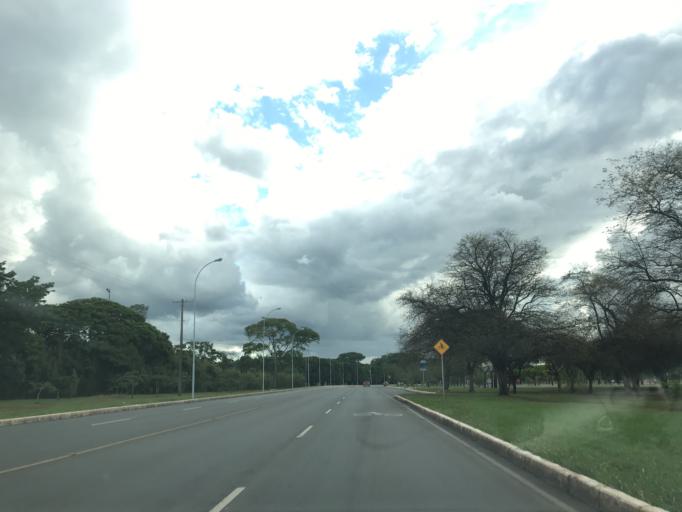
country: BR
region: Federal District
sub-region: Brasilia
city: Brasilia
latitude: -15.8050
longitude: -47.9108
